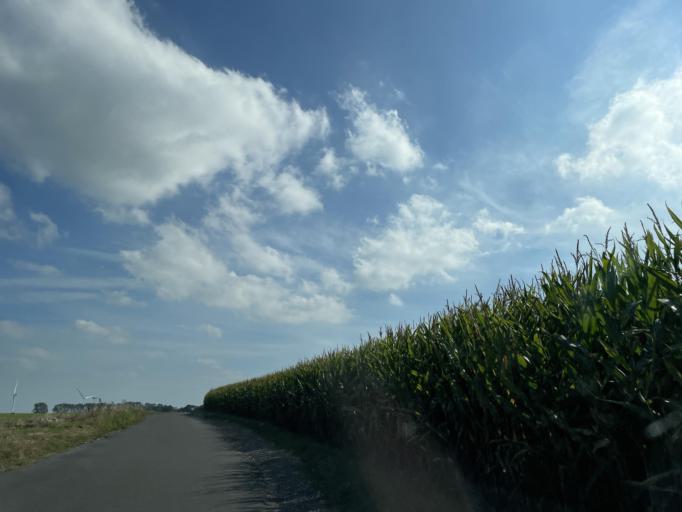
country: FR
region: Haute-Normandie
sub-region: Departement de la Seine-Maritime
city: Criel-sur-Mer
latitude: 50.0353
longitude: 1.3432
